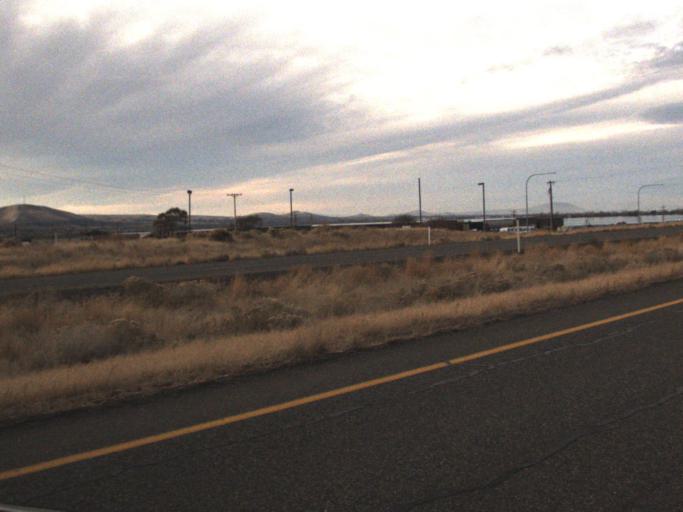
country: US
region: Washington
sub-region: Benton County
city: Finley
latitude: 46.1123
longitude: -118.9201
